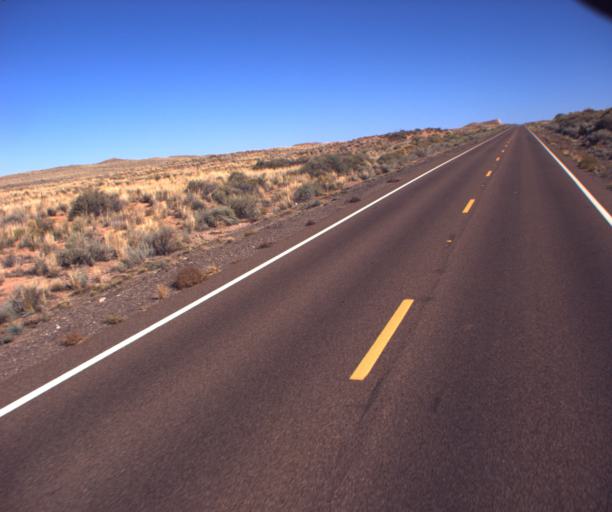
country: US
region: Arizona
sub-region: Navajo County
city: Winslow
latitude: 35.0606
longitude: -110.5846
